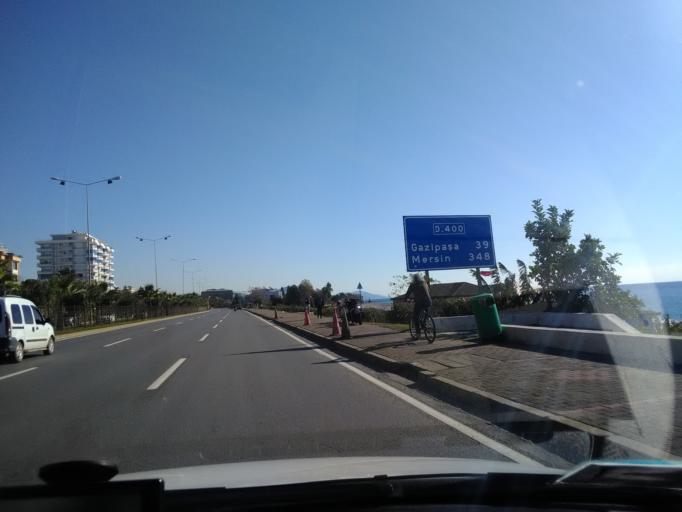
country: TR
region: Antalya
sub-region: Alanya
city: Mahmutlar
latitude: 36.5243
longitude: 32.0516
